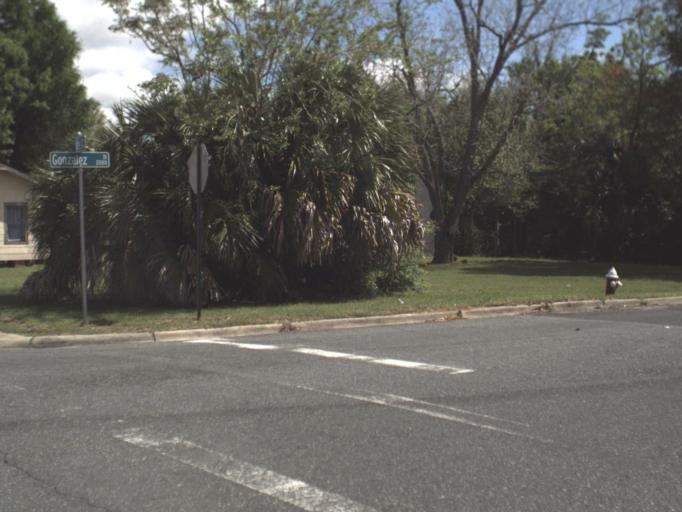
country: US
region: Florida
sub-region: Escambia County
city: Pensacola
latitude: 30.4236
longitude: -87.2410
